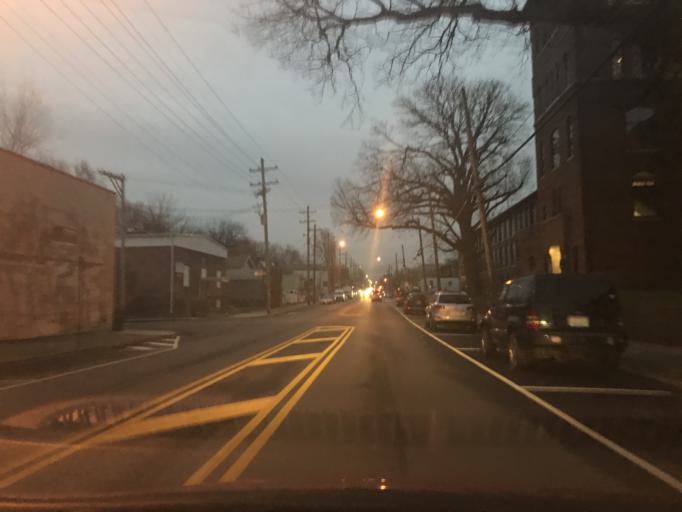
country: US
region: Kentucky
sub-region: Jefferson County
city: Audubon Park
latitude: 38.2298
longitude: -85.7395
